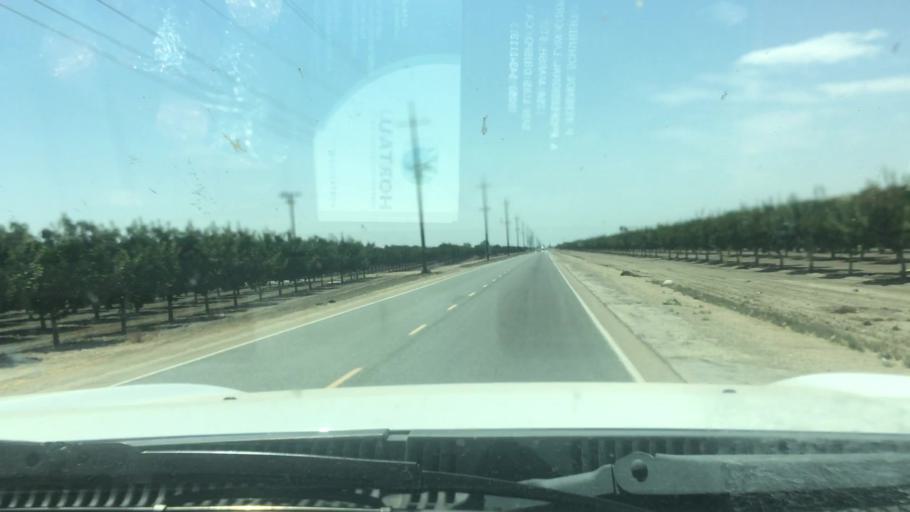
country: US
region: California
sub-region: Kings County
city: Corcoran
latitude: 36.0508
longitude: -119.5084
